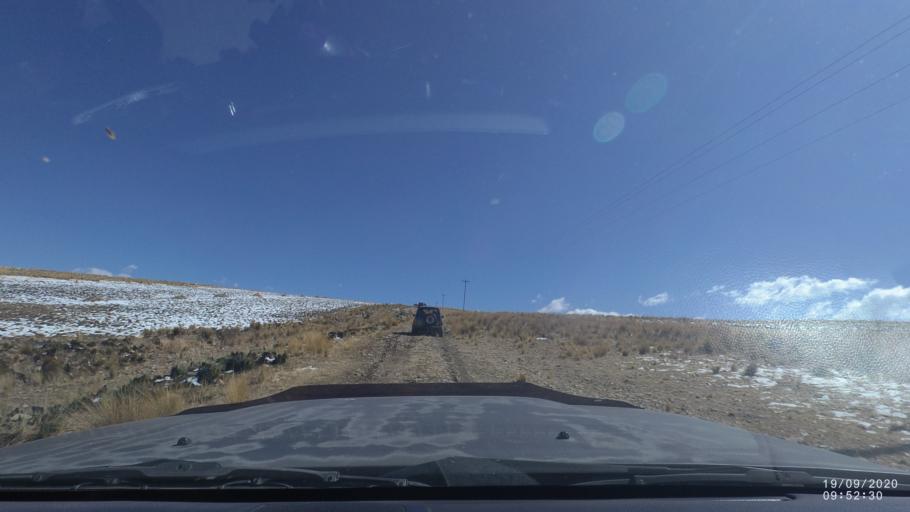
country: BO
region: Cochabamba
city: Cochabamba
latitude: -17.3184
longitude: -66.0813
